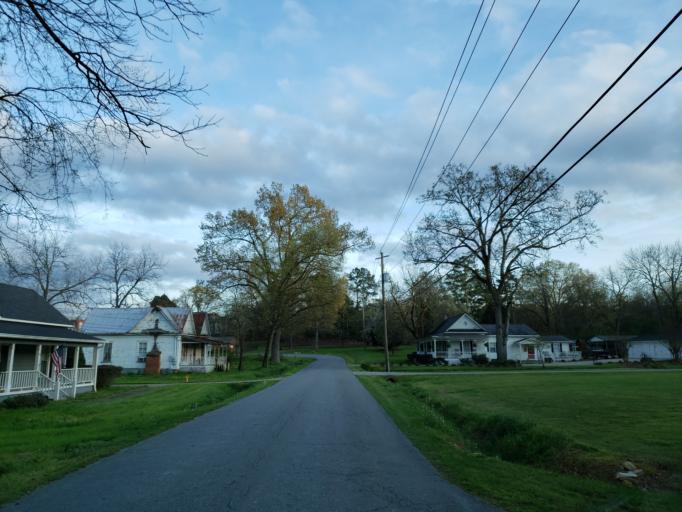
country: US
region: Georgia
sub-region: Polk County
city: Aragon
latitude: 34.0874
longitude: -84.9896
